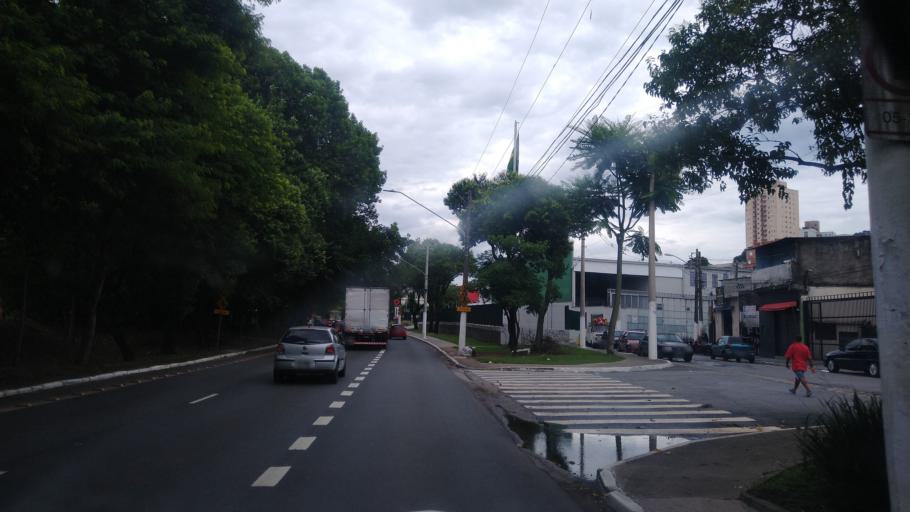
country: BR
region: Sao Paulo
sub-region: Guarulhos
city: Guarulhos
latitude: -23.5137
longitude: -46.5392
